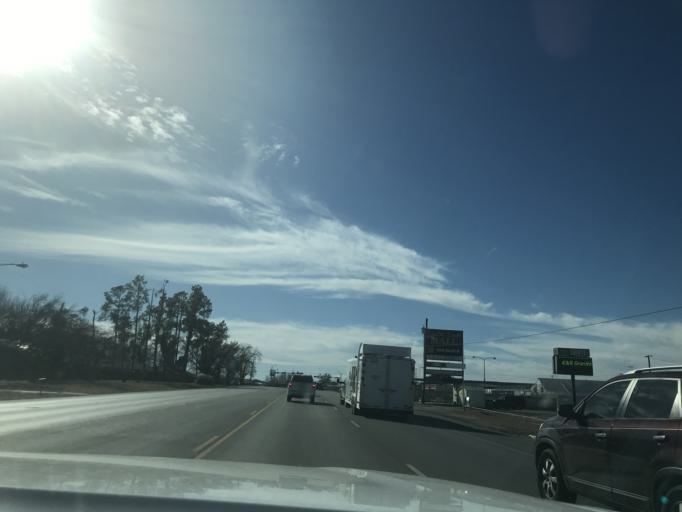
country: US
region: Texas
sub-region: Erath County
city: Stephenville
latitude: 32.2060
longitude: -98.2082
